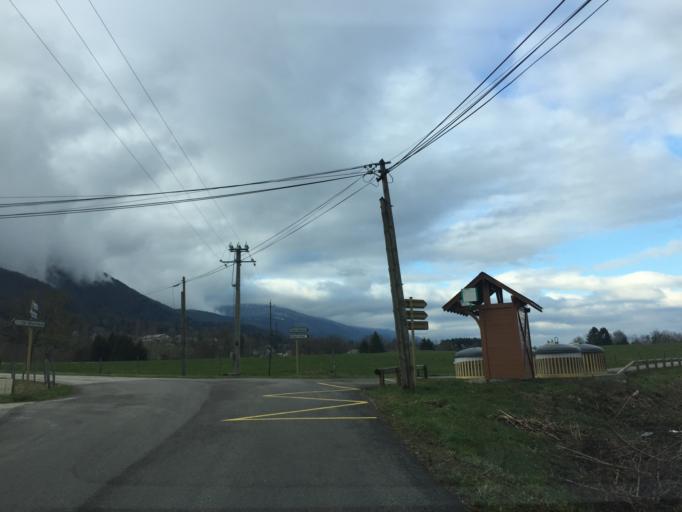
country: FR
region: Rhone-Alpes
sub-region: Departement de la Savoie
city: Vimines
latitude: 45.5404
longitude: 5.8519
